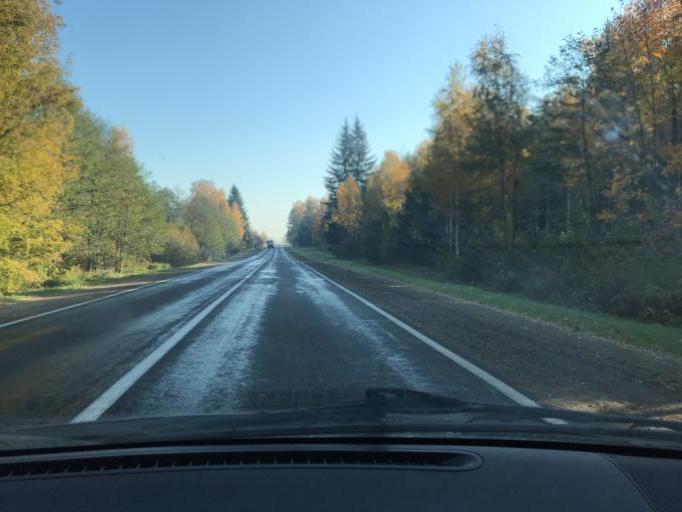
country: BY
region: Brest
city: Lyakhavichy
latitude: 52.9620
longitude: 26.4407
